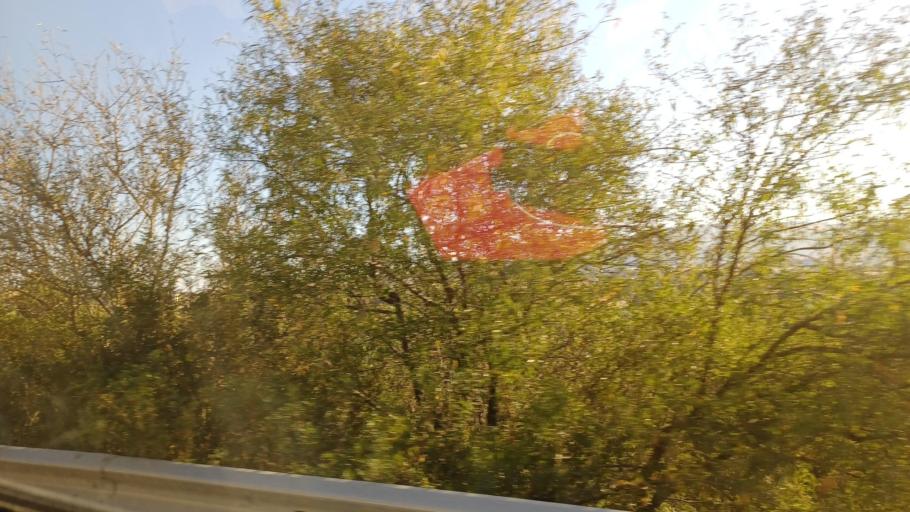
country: CY
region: Pafos
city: Polis
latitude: 34.9980
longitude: 32.4369
